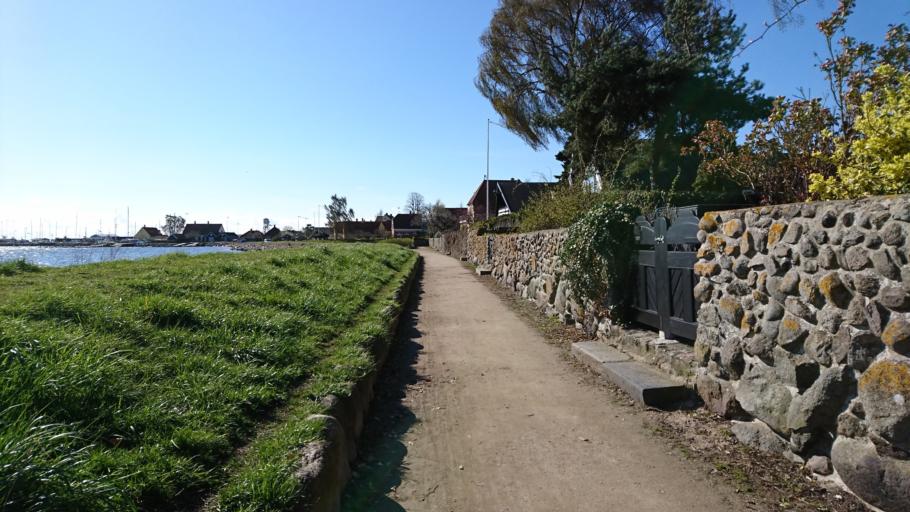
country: DK
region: Capital Region
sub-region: Dragor Kommune
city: Dragor
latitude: 55.5966
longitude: 12.6726
